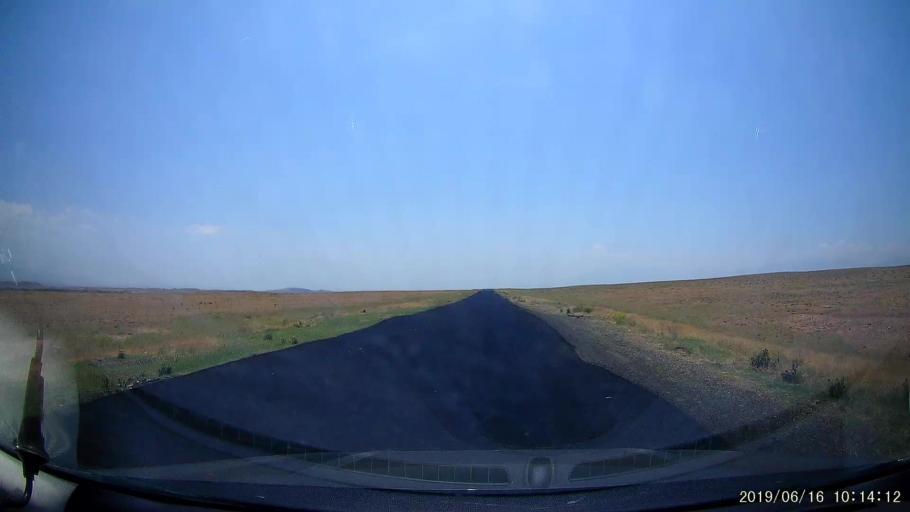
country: TR
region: Igdir
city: Tuzluca
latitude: 40.1870
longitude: 43.6576
